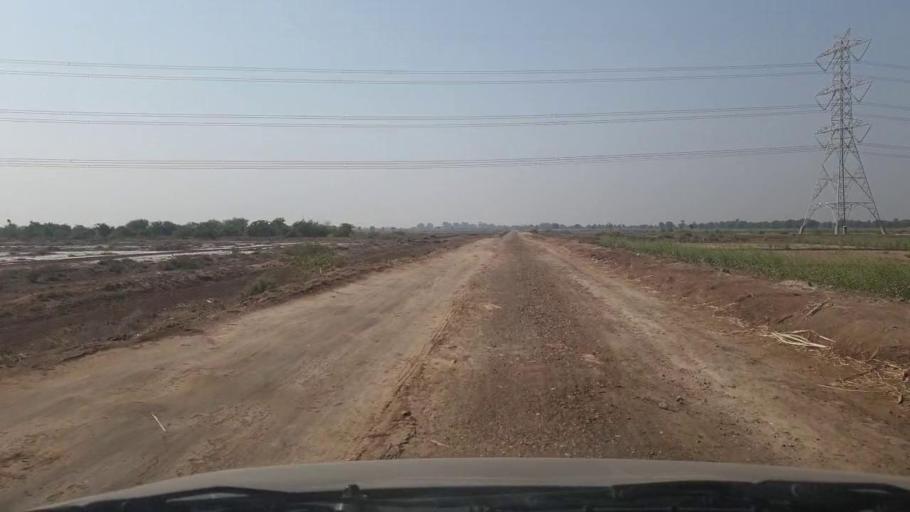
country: PK
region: Sindh
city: Mirwah Gorchani
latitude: 25.2426
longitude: 69.0988
